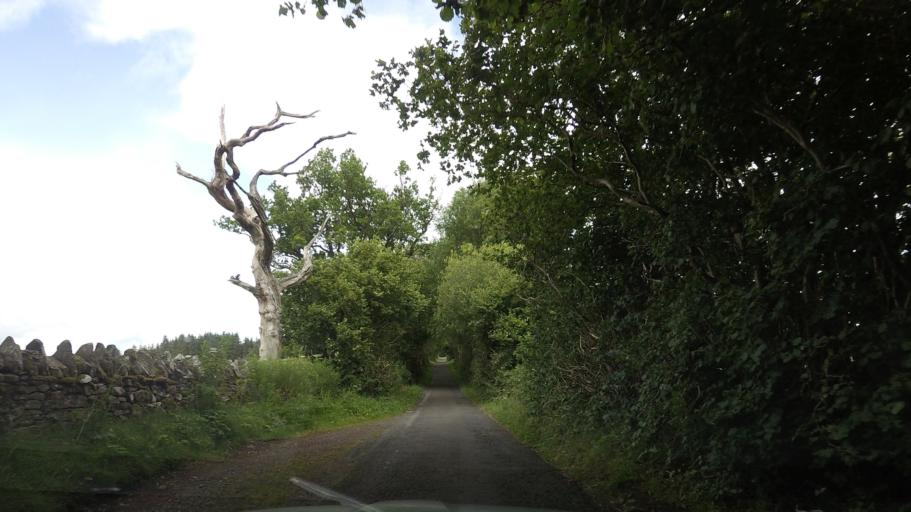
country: GB
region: Scotland
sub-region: Stirling
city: Killearn
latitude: 56.0786
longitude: -4.4499
